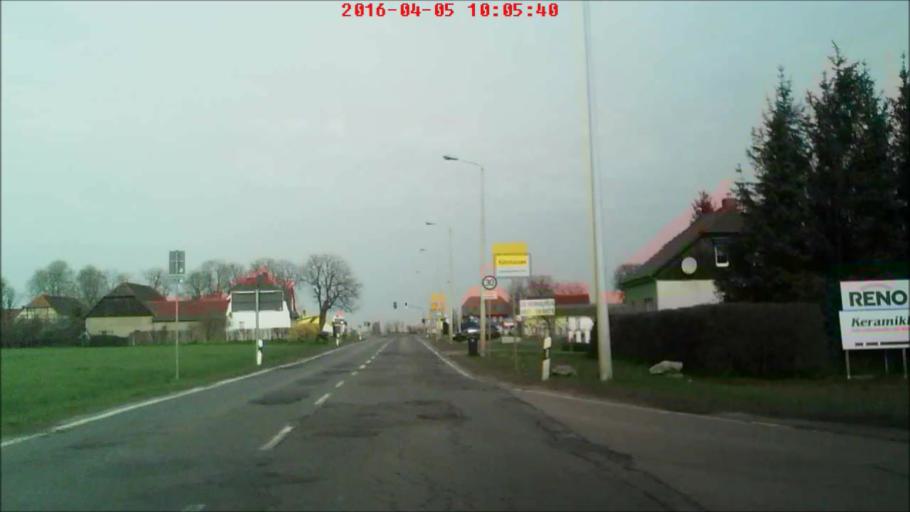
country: DE
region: Thuringia
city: Elxleben
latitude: 51.0313
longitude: 10.9713
